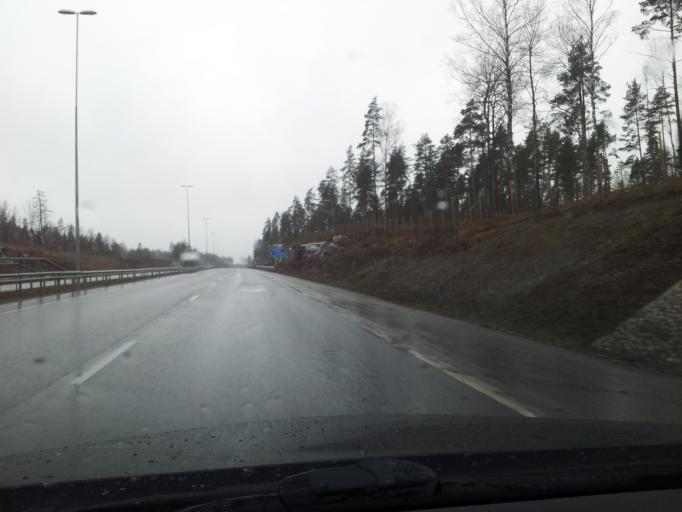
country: FI
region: Uusimaa
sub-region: Helsinki
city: Espoo
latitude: 60.1532
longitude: 24.5986
